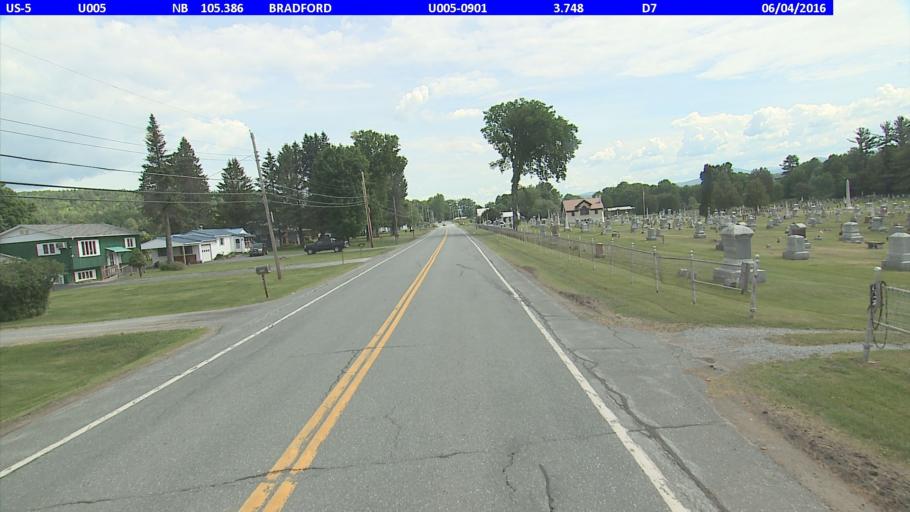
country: US
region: New Hampshire
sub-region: Grafton County
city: Haverhill
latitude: 44.0074
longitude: -72.1112
